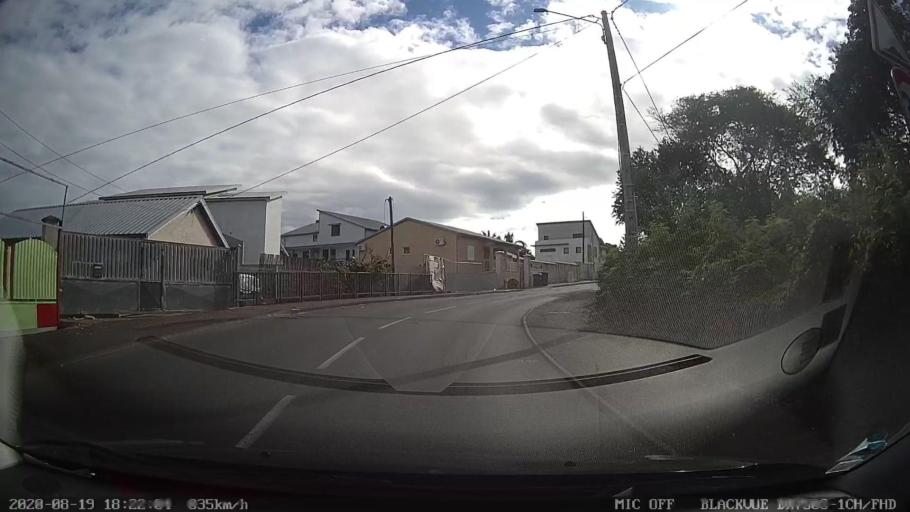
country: RE
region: Reunion
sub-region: Reunion
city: La Possession
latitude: -20.9556
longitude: 55.3373
